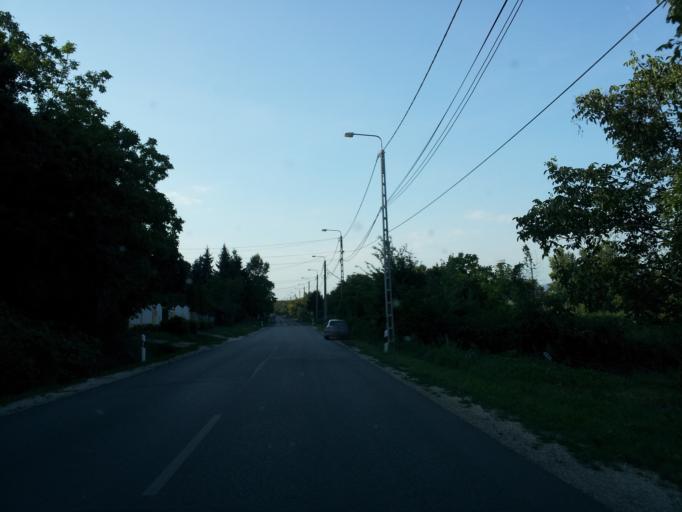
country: HU
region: Pest
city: Leanyfalu
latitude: 47.7328
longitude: 19.0885
